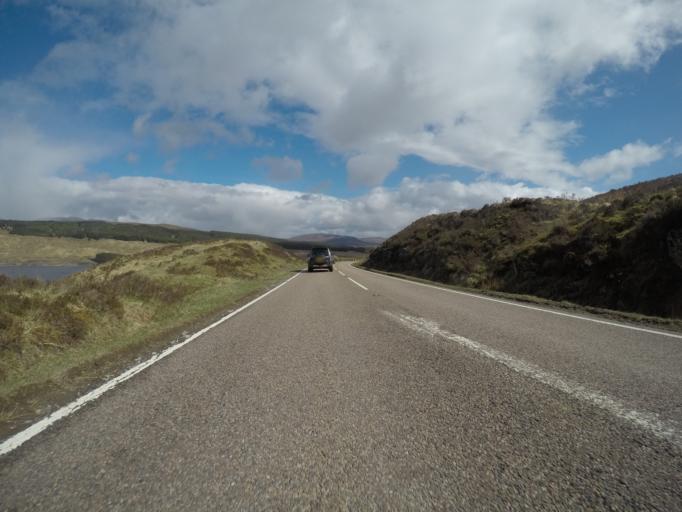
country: GB
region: Scotland
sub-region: Highland
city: Spean Bridge
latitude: 57.1229
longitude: -4.9716
